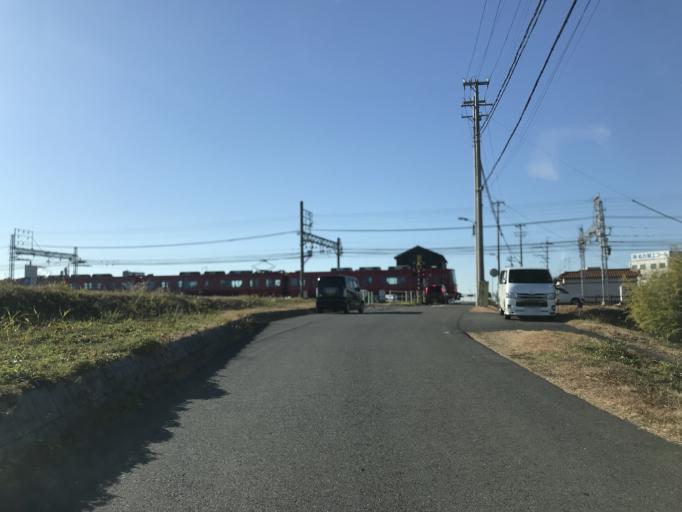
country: JP
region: Aichi
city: Nagoya-shi
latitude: 35.1949
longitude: 136.8691
